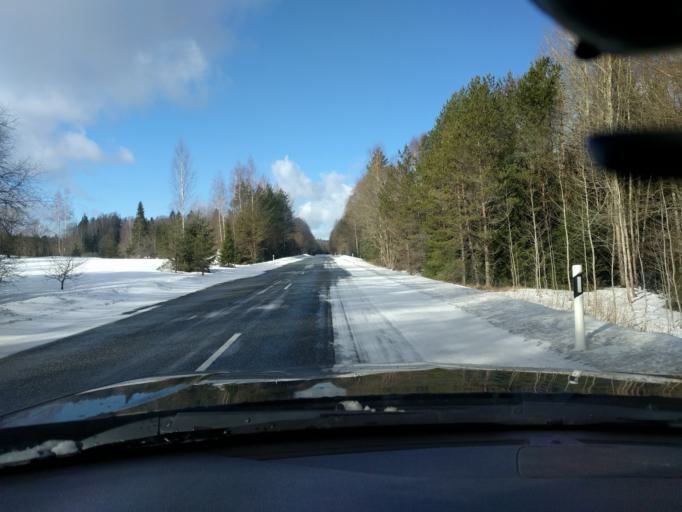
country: EE
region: Harju
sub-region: Anija vald
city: Kehra
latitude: 59.2130
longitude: 25.5010
